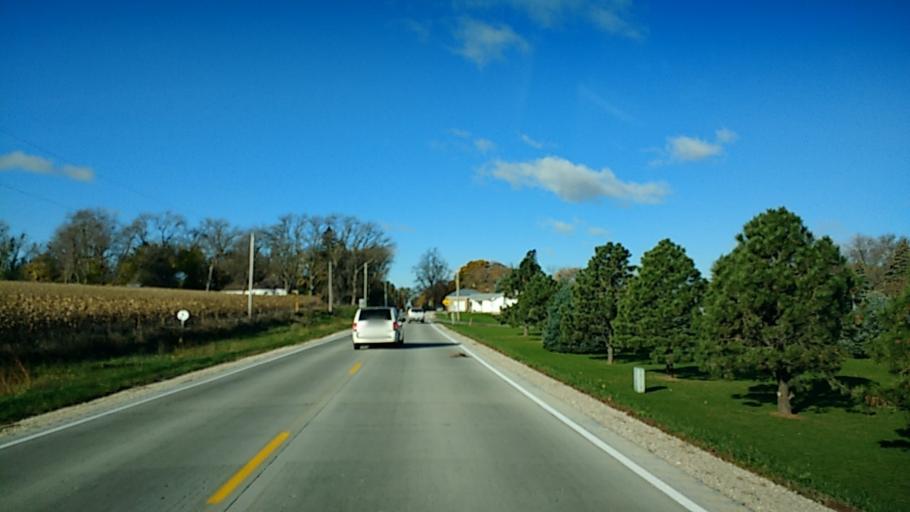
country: US
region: Iowa
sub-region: Ida County
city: Holstein
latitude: 42.5038
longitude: -95.4130
